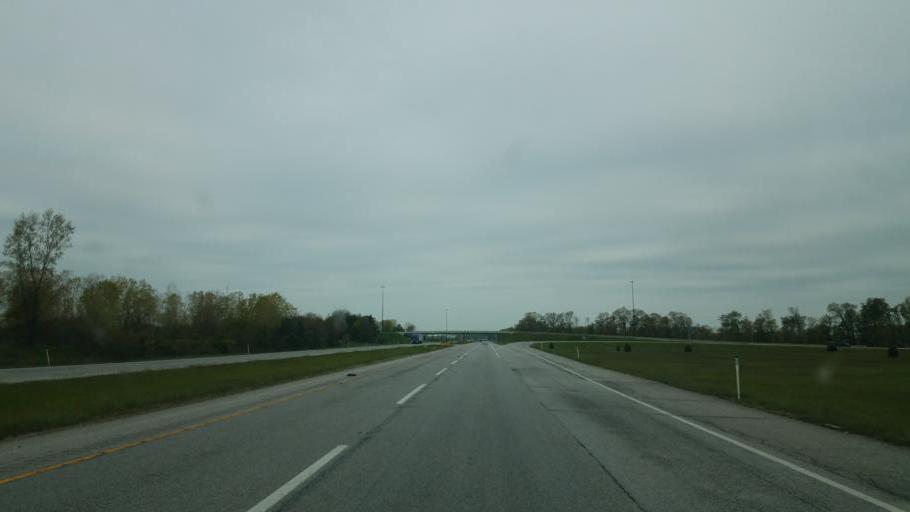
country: US
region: Michigan
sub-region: Saint Joseph County
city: White Pigeon
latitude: 41.7473
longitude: -85.6815
